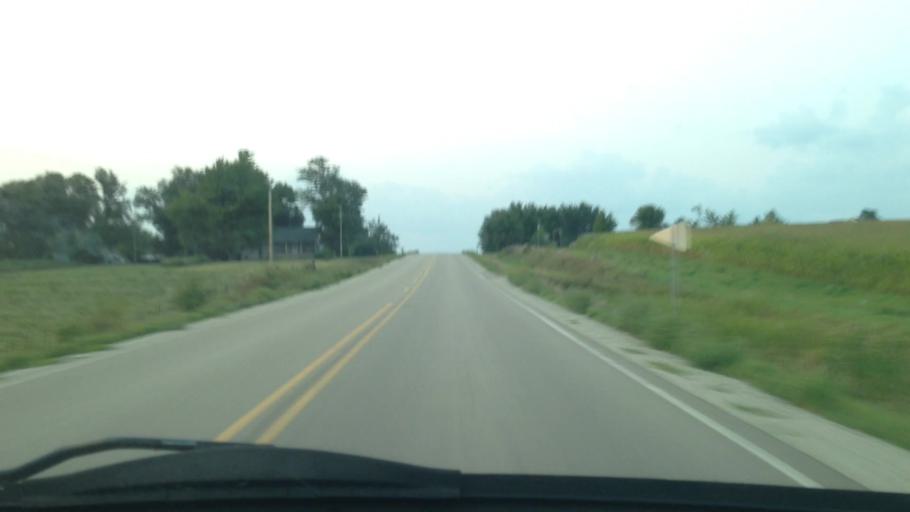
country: US
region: Iowa
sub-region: Benton County
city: Urbana
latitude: 42.2088
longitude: -91.8716
